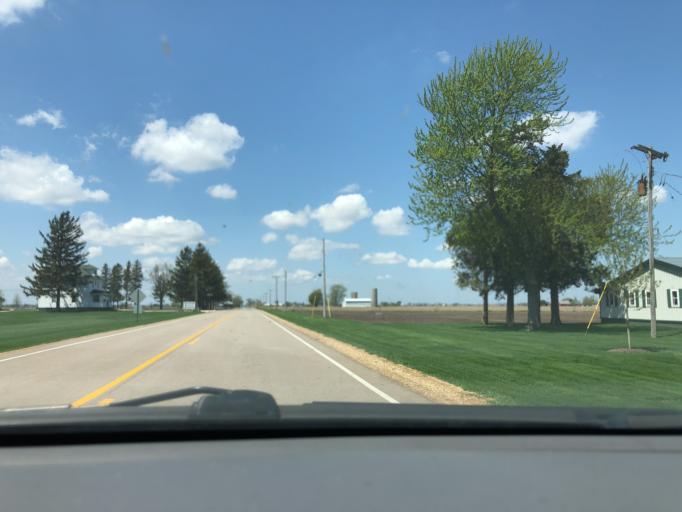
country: US
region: Illinois
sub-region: Kane County
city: Hampshire
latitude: 42.1100
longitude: -88.5609
